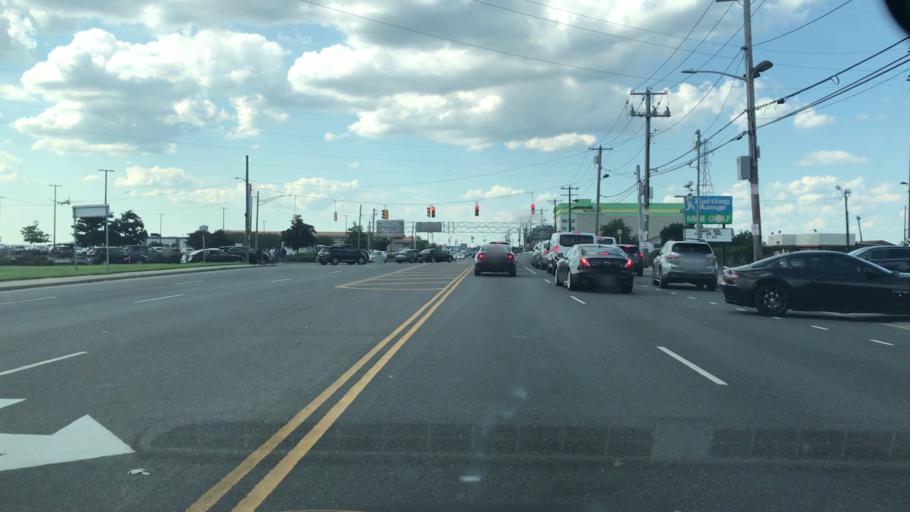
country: US
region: New York
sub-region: Nassau County
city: Inwood
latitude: 40.6297
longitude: -73.7377
